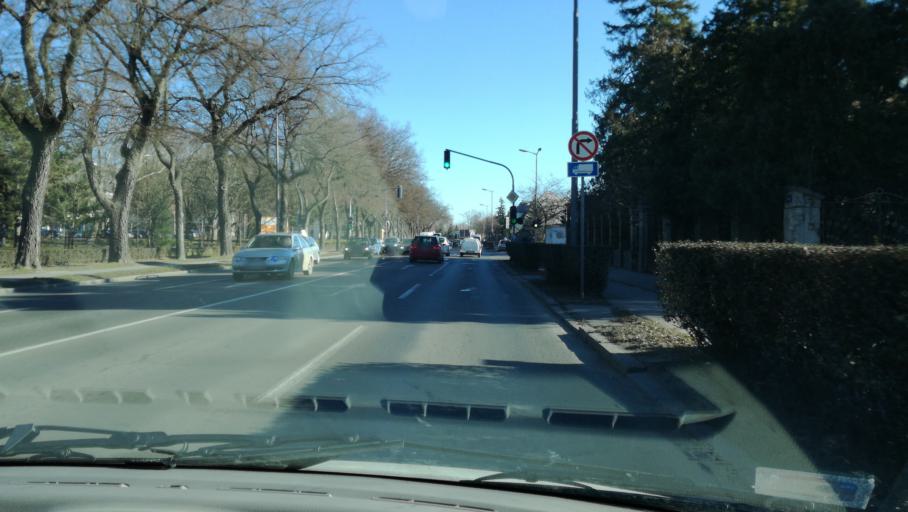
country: RS
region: Autonomna Pokrajina Vojvodina
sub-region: Severnobacki Okrug
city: Subotica
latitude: 46.1000
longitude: 19.6815
